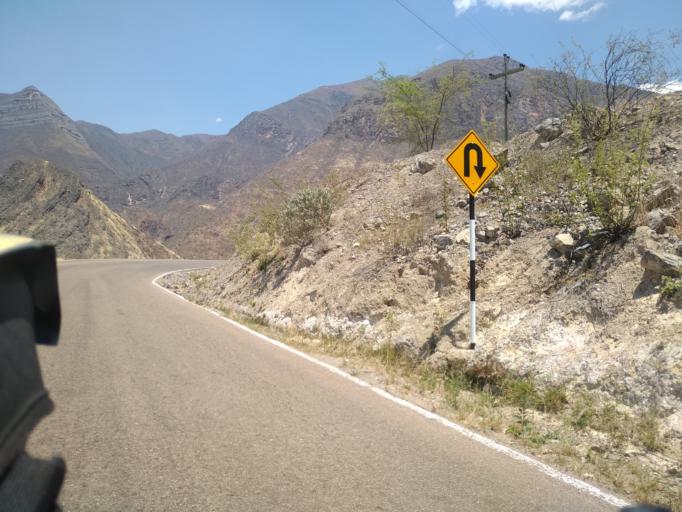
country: PE
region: Amazonas
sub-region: Provincia de Chachapoyas
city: Balsas
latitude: -6.8473
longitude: -78.0396
